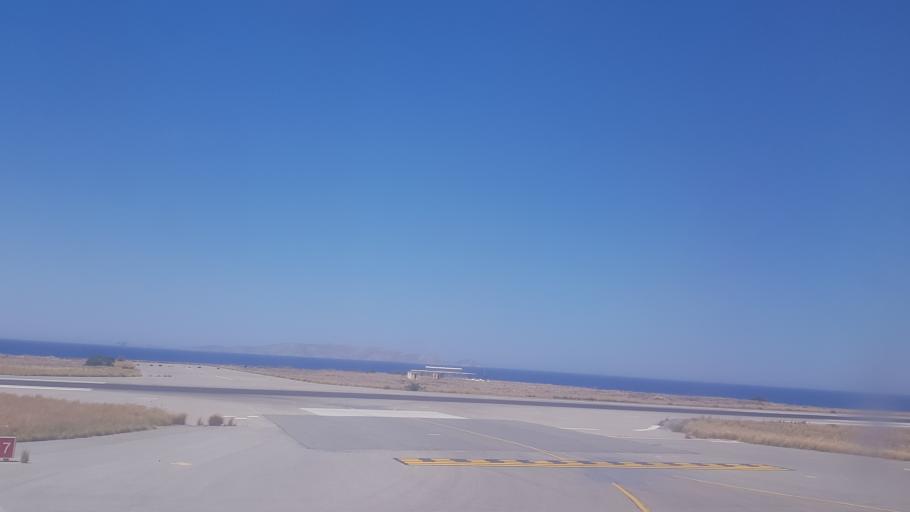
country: GR
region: Crete
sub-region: Nomos Irakleiou
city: Nea Alikarnassos
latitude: 35.3385
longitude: 25.1837
